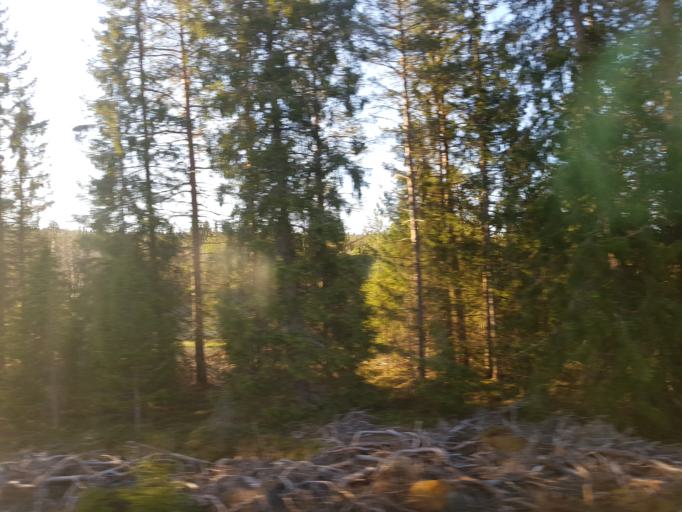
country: NO
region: Sor-Trondelag
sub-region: Rennebu
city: Berkak
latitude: 62.8785
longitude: 10.0942
